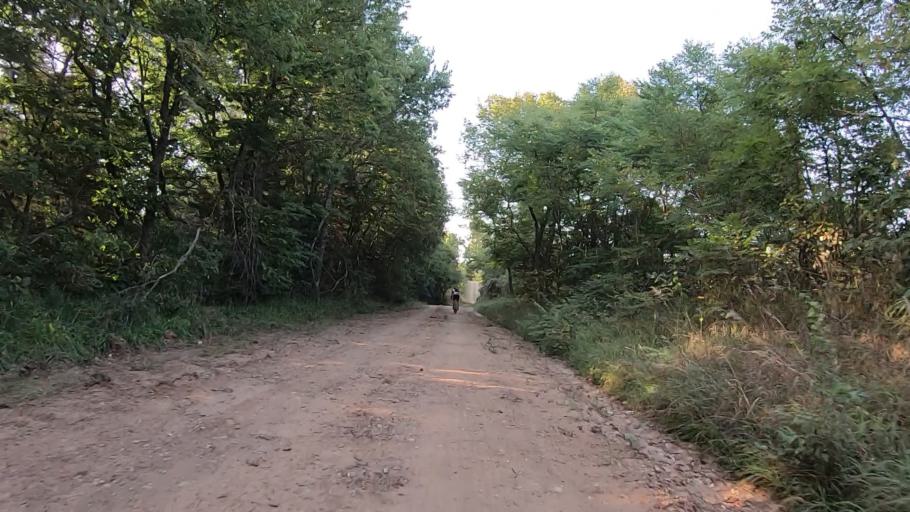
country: US
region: Kansas
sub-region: Marshall County
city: Blue Rapids
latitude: 39.7580
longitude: -96.7507
